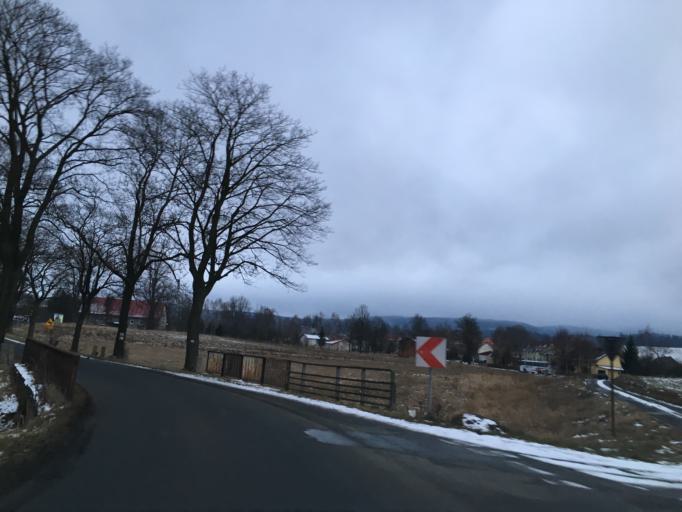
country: PL
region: Lower Silesian Voivodeship
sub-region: Powiat kamiennogorski
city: Krzeszow
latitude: 50.7094
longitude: 16.1014
